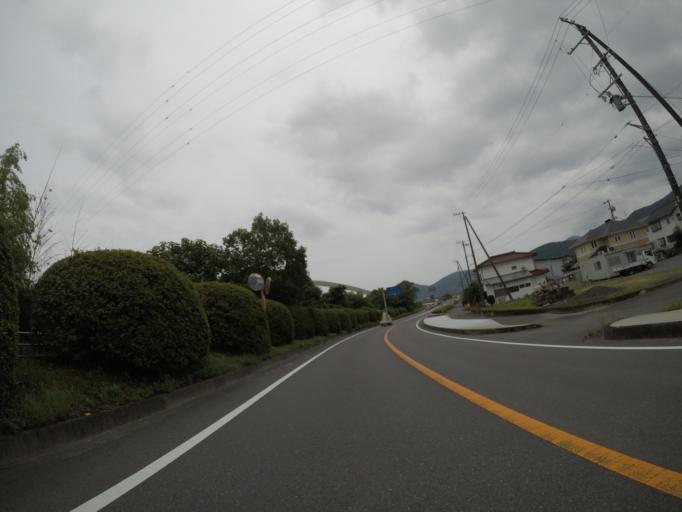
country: JP
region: Shizuoka
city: Fujinomiya
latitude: 35.1946
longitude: 138.5879
